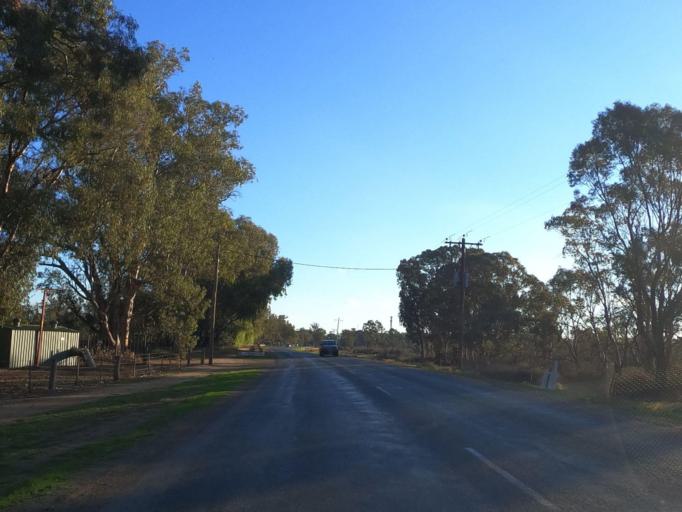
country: AU
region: Victoria
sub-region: Swan Hill
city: Swan Hill
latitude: -35.3362
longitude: 143.5743
